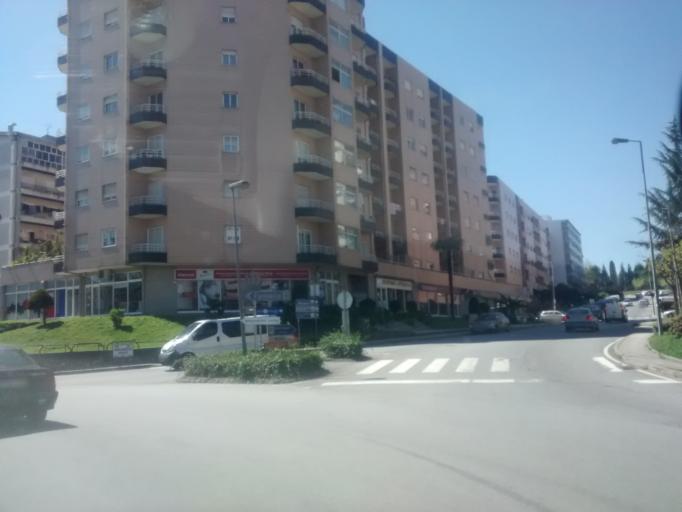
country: PT
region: Braga
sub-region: Braga
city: Braga
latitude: 41.5603
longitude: -8.4075
